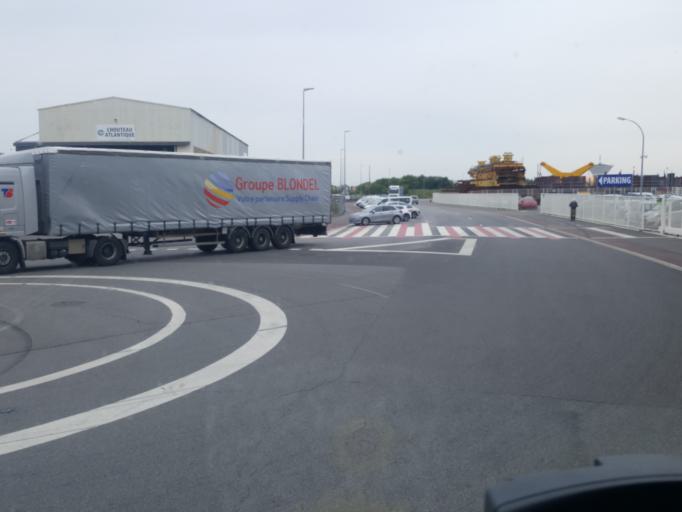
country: FR
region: Pays de la Loire
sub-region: Departement de la Loire-Atlantique
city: Saint-Nazaire
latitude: 47.2895
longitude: -2.1925
